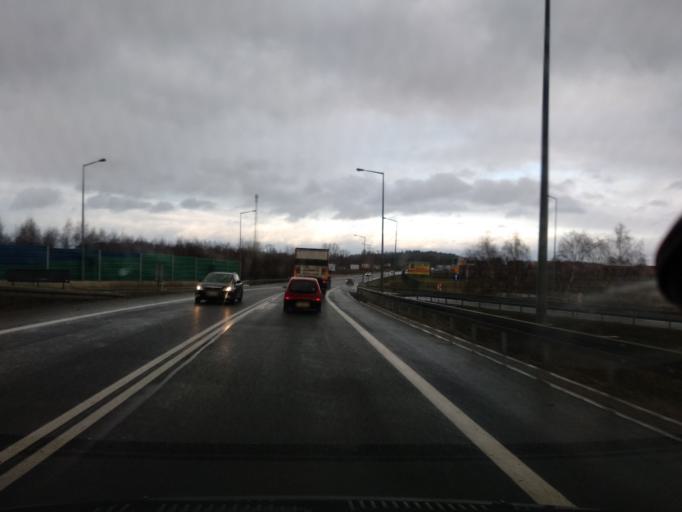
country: PL
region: Greater Poland Voivodeship
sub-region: Powiat koninski
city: Stare Miasto
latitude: 52.1649
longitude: 18.2074
